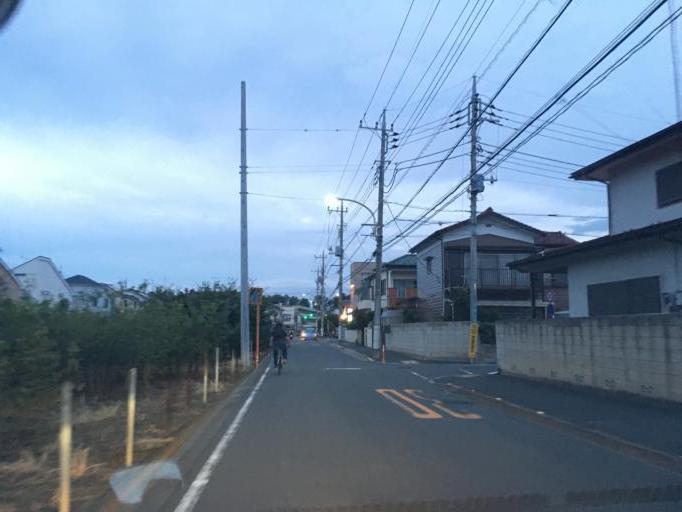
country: JP
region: Tokyo
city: Kokubunji
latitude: 35.7195
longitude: 139.4564
